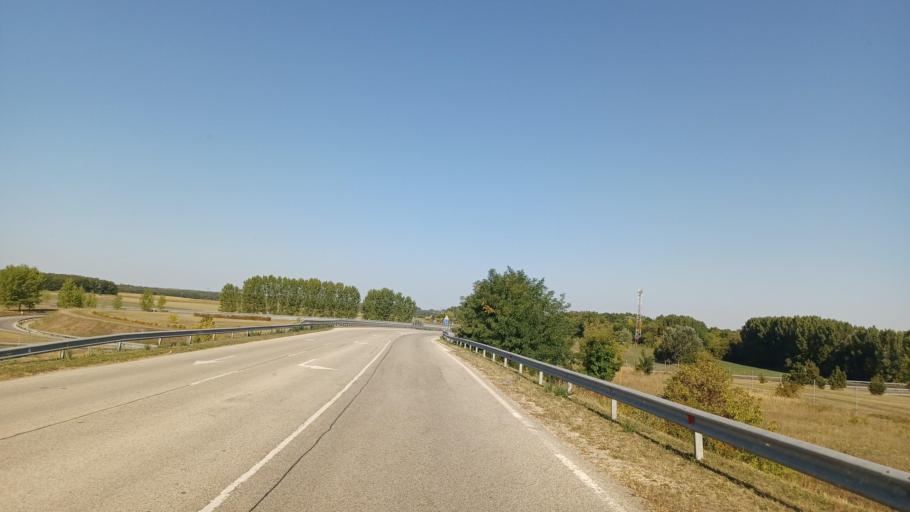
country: HU
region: Tolna
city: Paks
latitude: 46.6714
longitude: 18.8166
